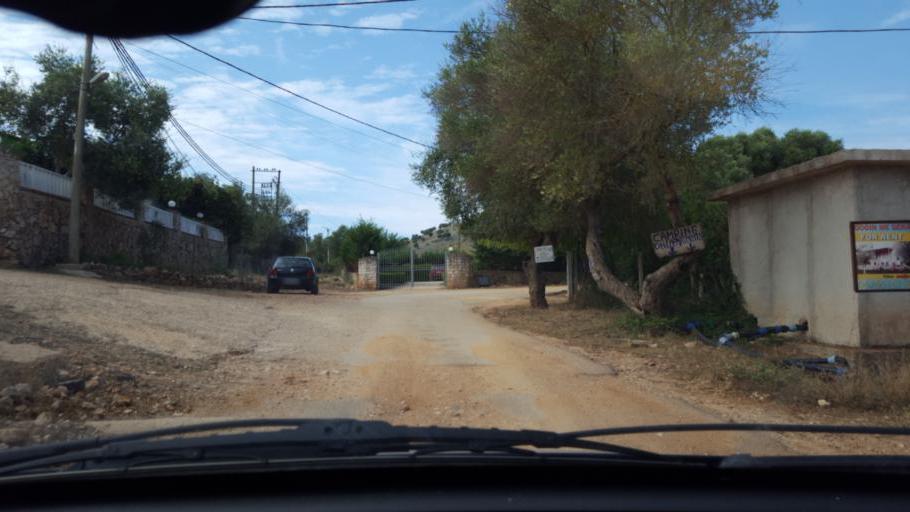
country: AL
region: Vlore
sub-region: Rrethi i Sarandes
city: Xarre
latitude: 39.7634
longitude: 19.9926
